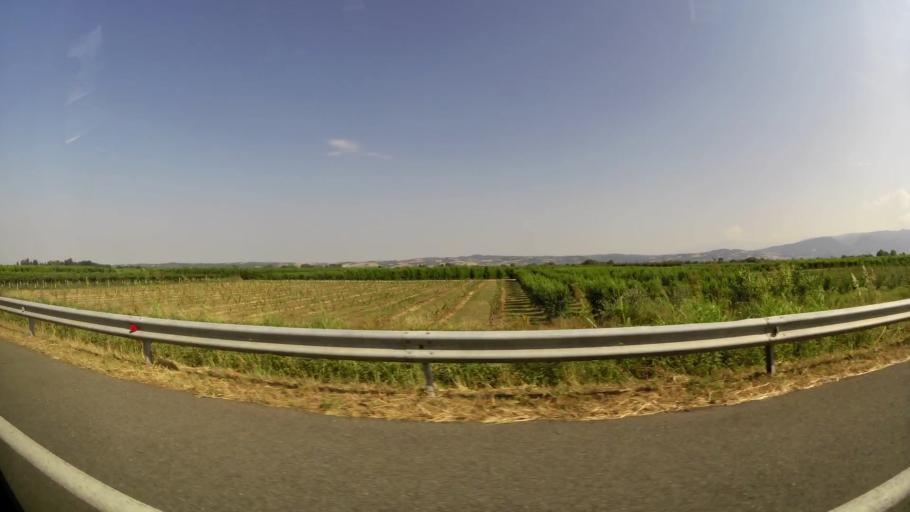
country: GR
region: Central Macedonia
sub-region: Nomos Imathias
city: Loutros
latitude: 40.5706
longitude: 22.3853
